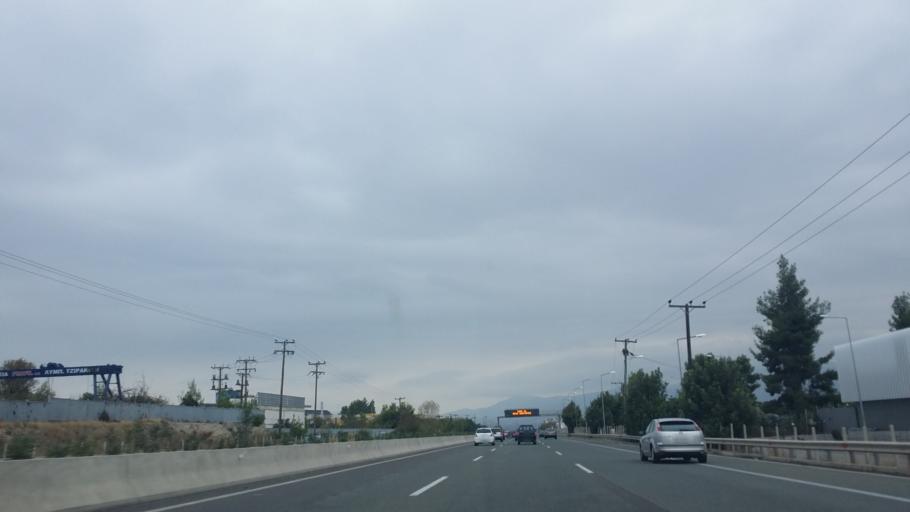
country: GR
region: Central Greece
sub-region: Nomos Voiotias
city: Oinofyta
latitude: 38.3178
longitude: 23.6266
